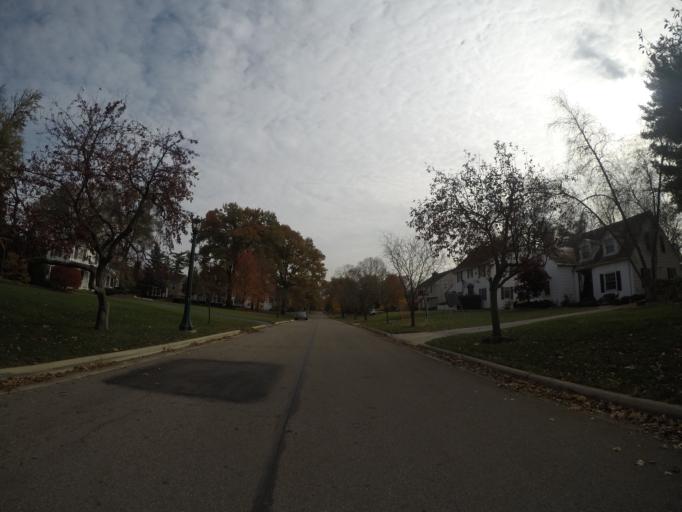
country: US
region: Ohio
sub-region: Franklin County
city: Upper Arlington
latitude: 40.0065
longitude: -83.0617
